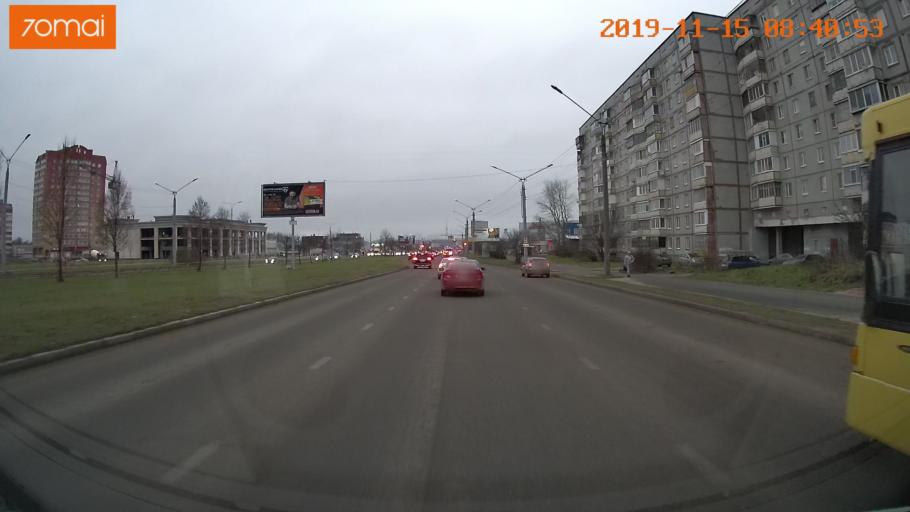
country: RU
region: Vologda
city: Cherepovets
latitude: 59.0963
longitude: 37.9128
